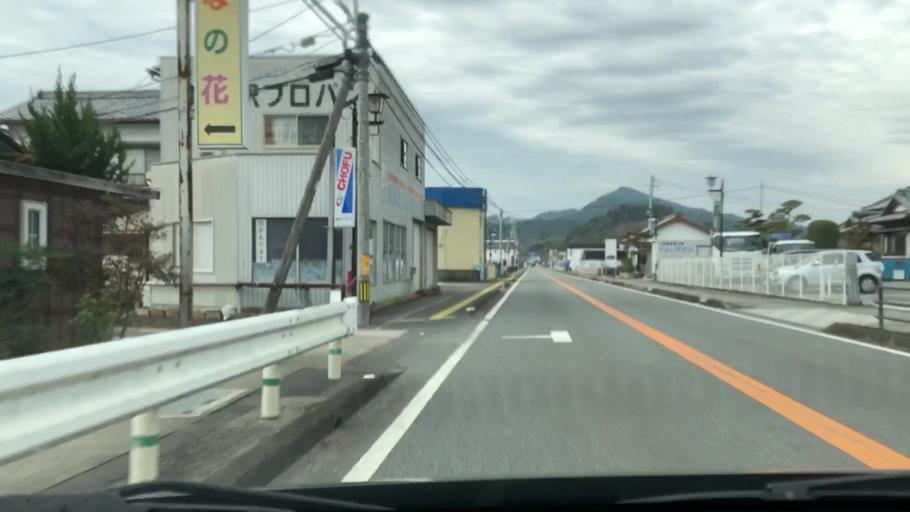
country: JP
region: Oita
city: Saiki
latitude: 32.9742
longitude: 131.8429
